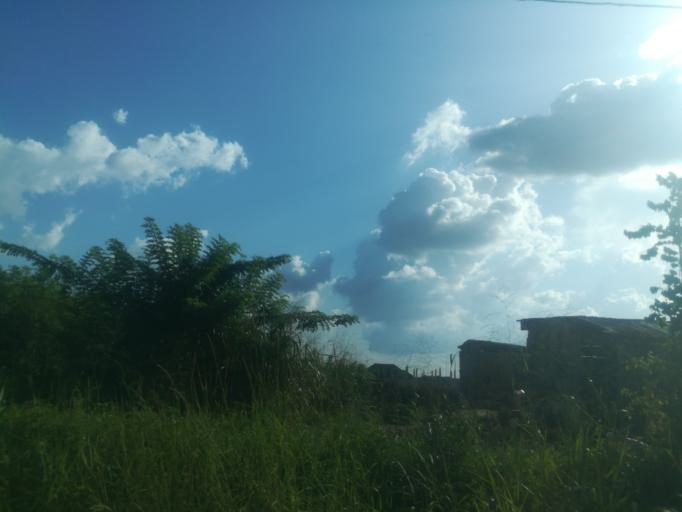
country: NG
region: Oyo
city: Egbeda
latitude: 7.4332
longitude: 3.9783
